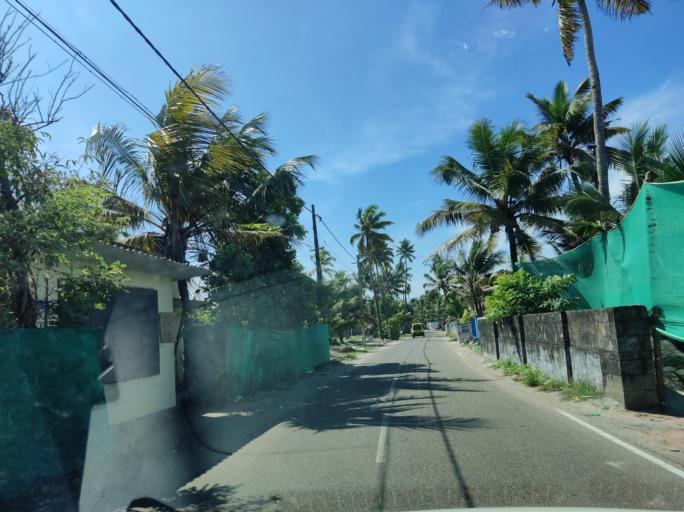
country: IN
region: Kerala
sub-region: Alappuzha
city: Kayankulam
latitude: 9.2192
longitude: 76.4257
